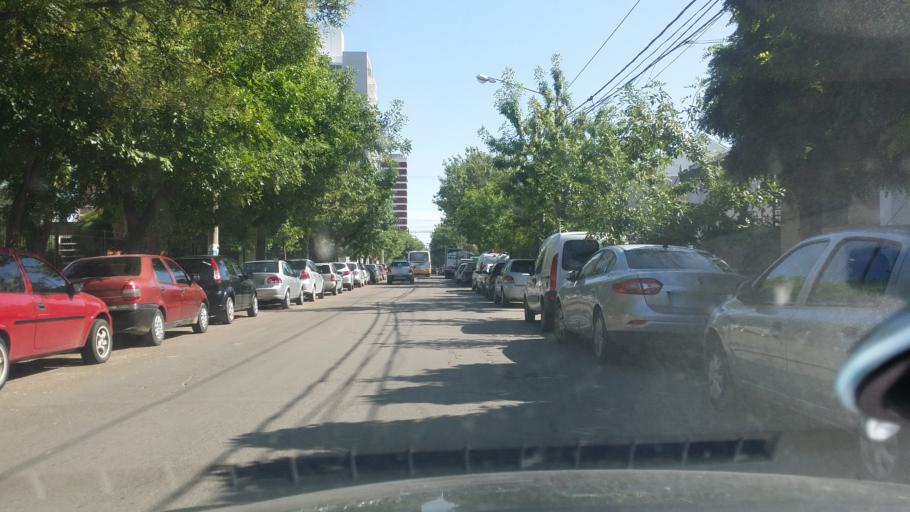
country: AR
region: La Pampa
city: Santa Rosa
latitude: -36.6230
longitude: -64.2873
